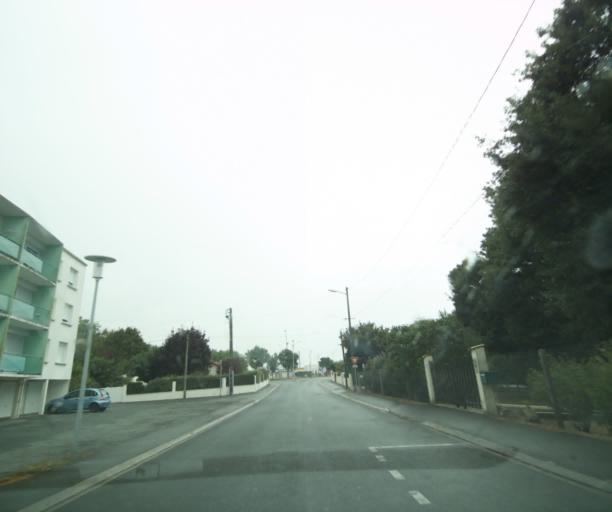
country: FR
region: Poitou-Charentes
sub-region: Departement de la Charente-Maritime
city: Tonnay-Charente
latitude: 45.9460
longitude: -0.9117
